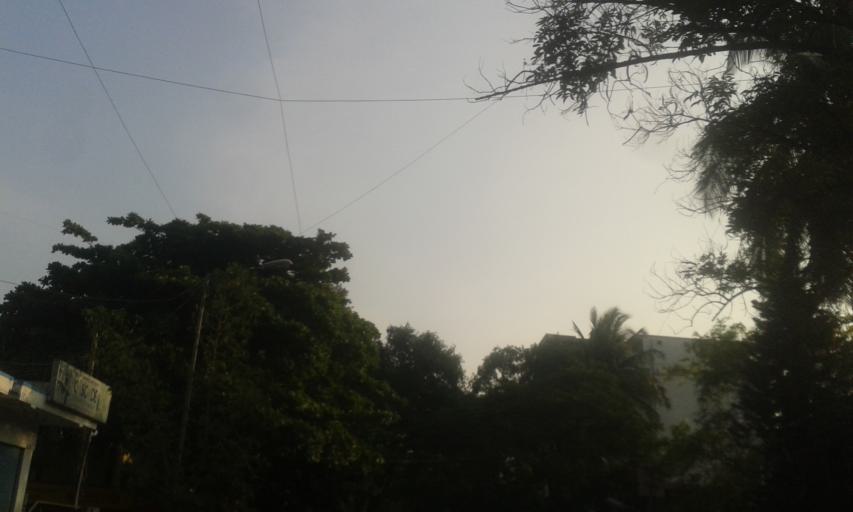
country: IN
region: Karnataka
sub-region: Bangalore Urban
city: Bangalore
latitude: 12.9112
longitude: 77.5952
